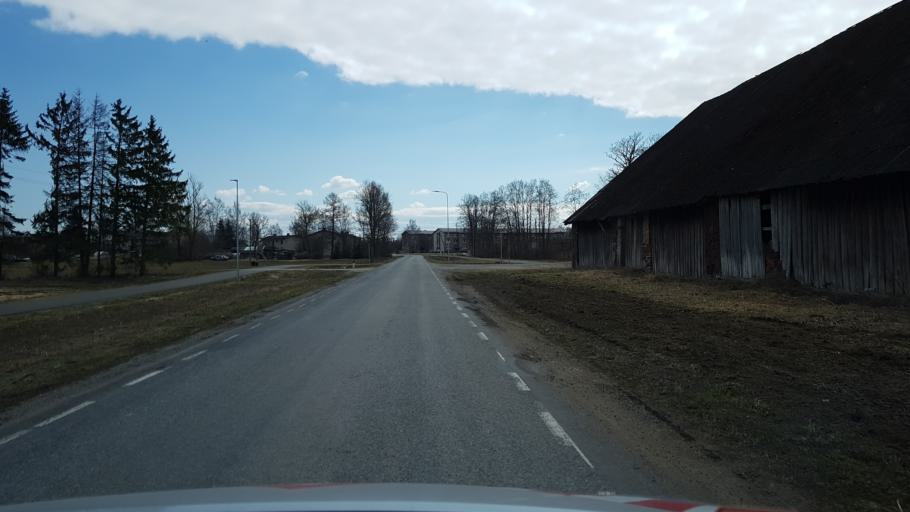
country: EE
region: Laeaene-Virumaa
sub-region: Haljala vald
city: Haljala
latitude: 59.4001
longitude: 26.2716
